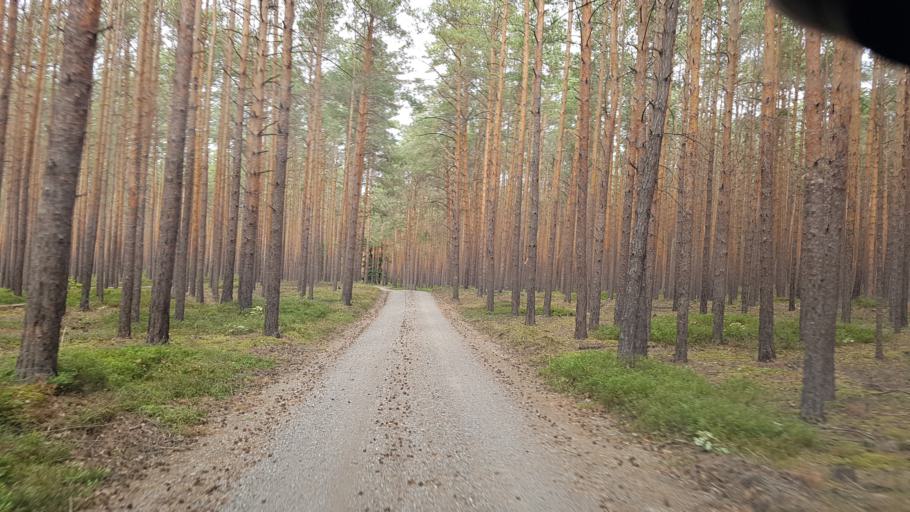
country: DE
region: Brandenburg
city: Ruckersdorf
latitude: 51.5713
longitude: 13.6188
